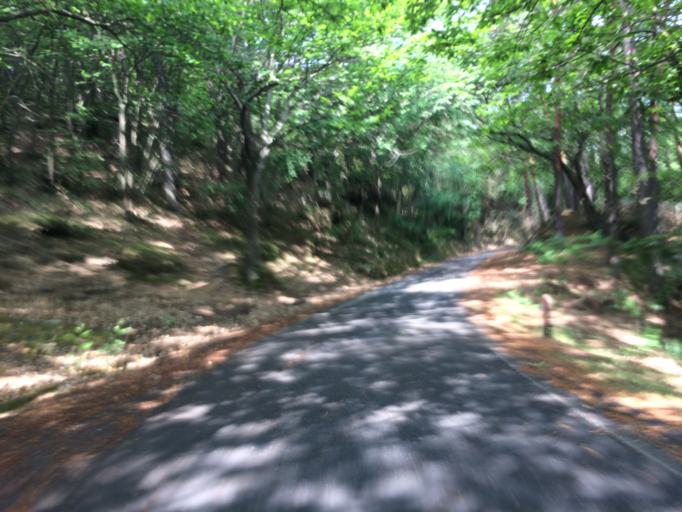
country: IT
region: Liguria
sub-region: Provincia di Imperia
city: Bajardo
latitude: 43.8960
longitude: 7.7312
